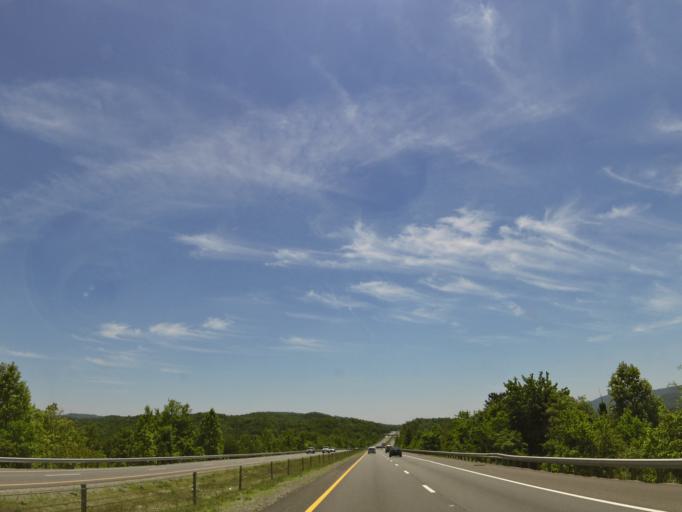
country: US
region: Tennessee
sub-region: Campbell County
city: Jacksboro
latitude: 36.4254
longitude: -84.2898
